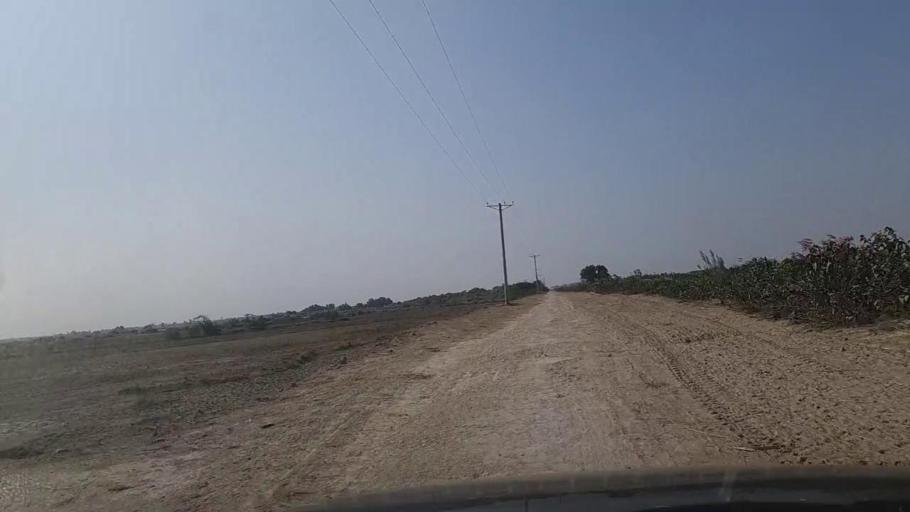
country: PK
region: Sindh
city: Gharo
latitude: 24.6900
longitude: 67.6093
